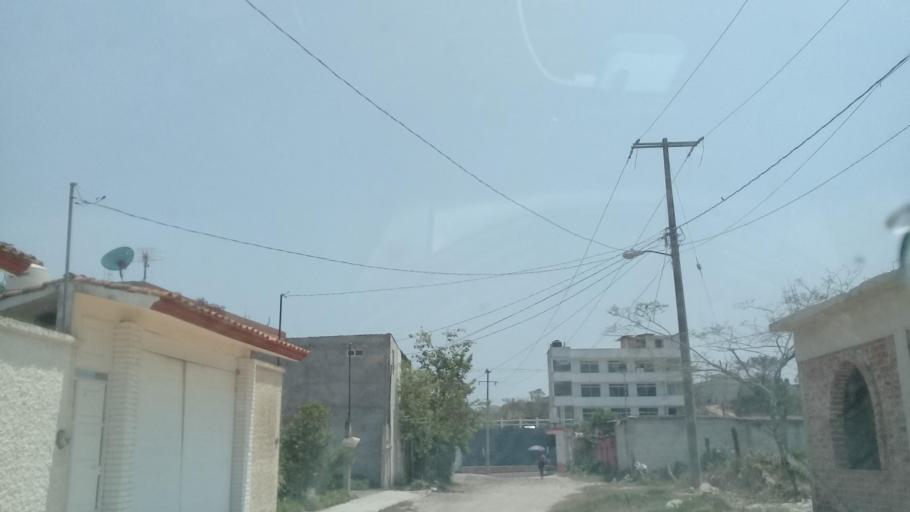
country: MX
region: Veracruz
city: El Castillo
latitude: 19.5553
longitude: -96.8551
